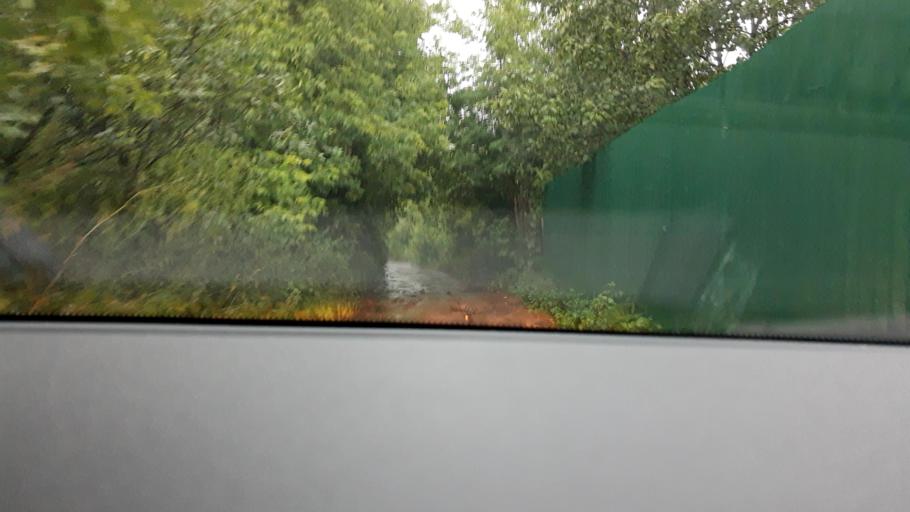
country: RU
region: Nizjnij Novgorod
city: Gorbatovka
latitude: 56.2609
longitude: 43.8264
